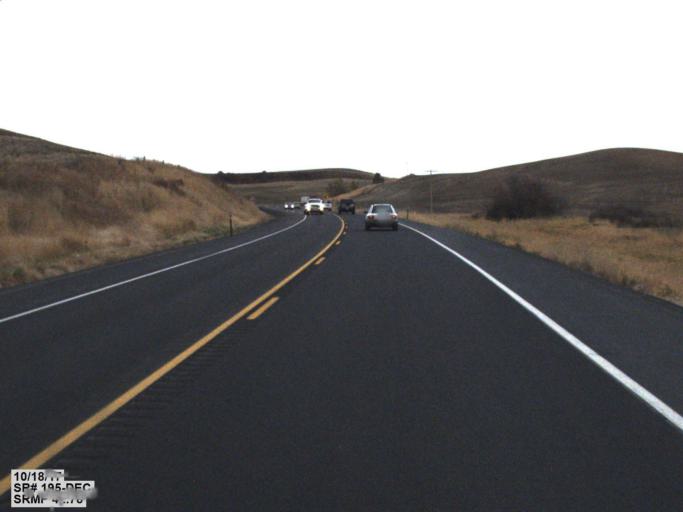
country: US
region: Washington
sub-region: Whitman County
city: Colfax
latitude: 46.9424
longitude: -117.3350
